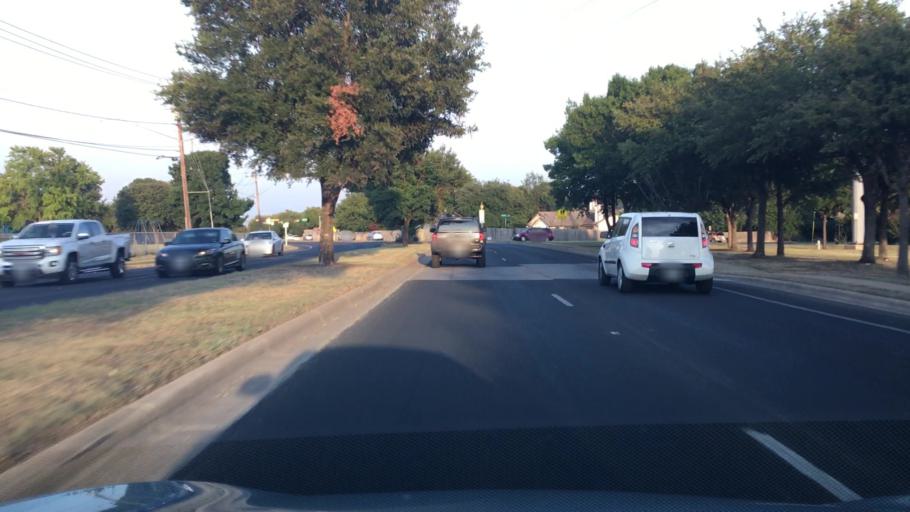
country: US
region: Texas
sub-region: Travis County
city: Shady Hollow
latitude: 30.1770
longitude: -97.8362
